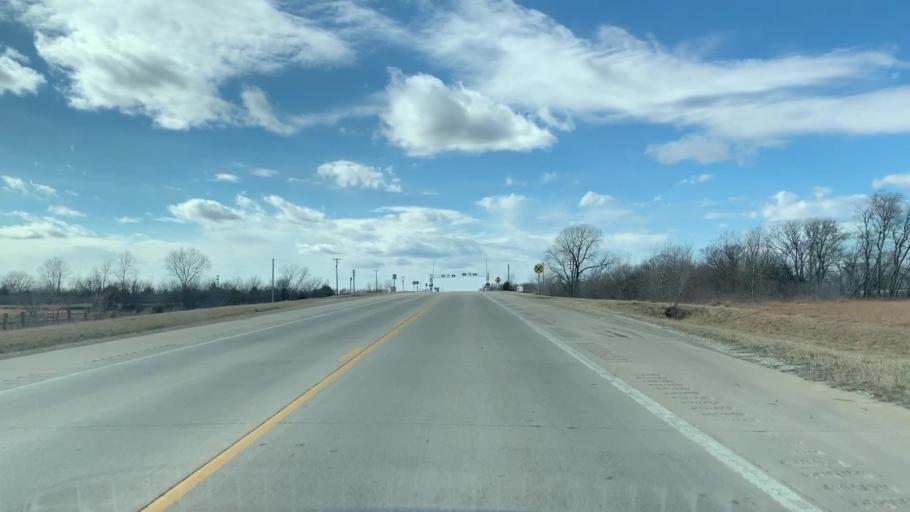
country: US
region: Kansas
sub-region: Neosho County
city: Chanute
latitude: 37.5288
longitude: -95.4674
